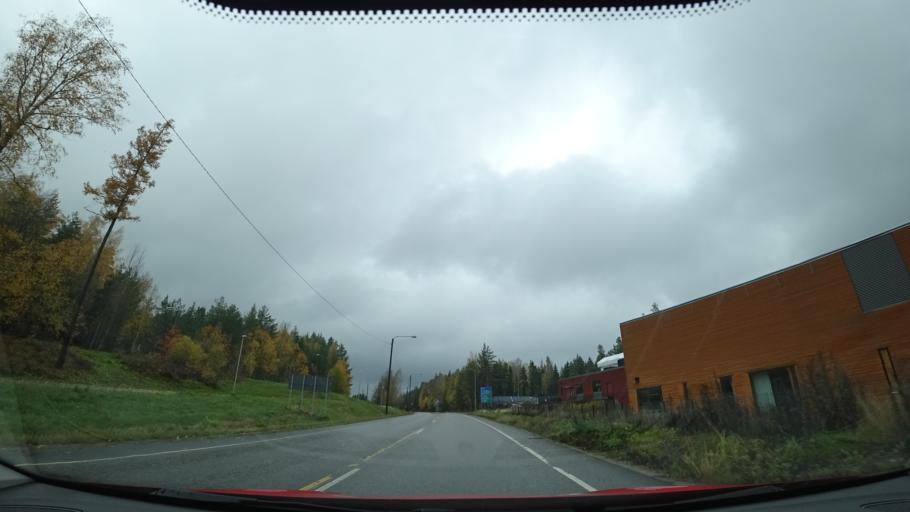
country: FI
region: Uusimaa
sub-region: Helsinki
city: Sibbo
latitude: 60.2619
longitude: 25.2104
